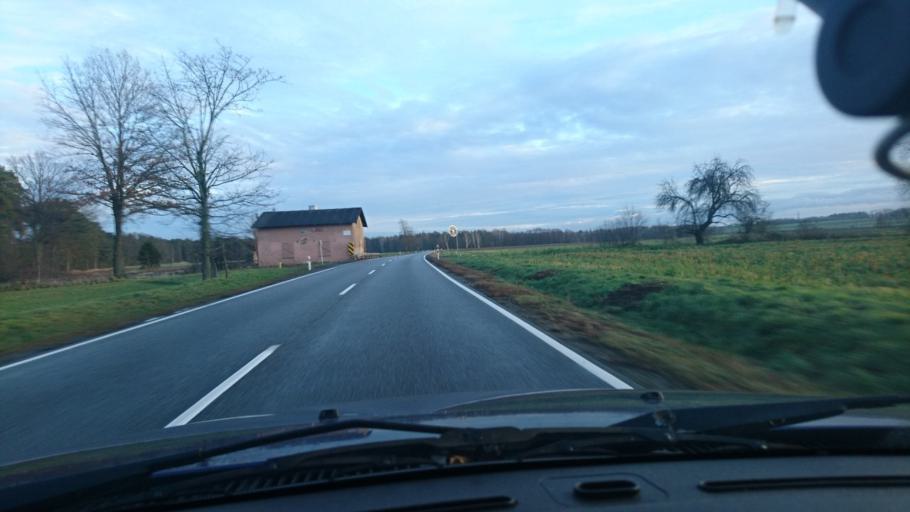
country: PL
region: Lodz Voivodeship
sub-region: Powiat wieruszowski
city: Boleslawiec
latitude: 51.1535
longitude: 18.1789
